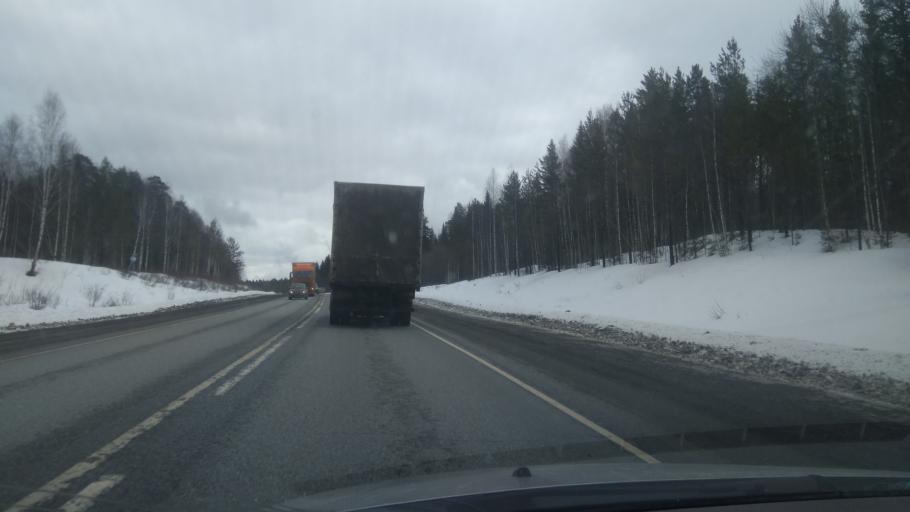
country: RU
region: Sverdlovsk
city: Atig
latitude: 56.7997
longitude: 59.3862
